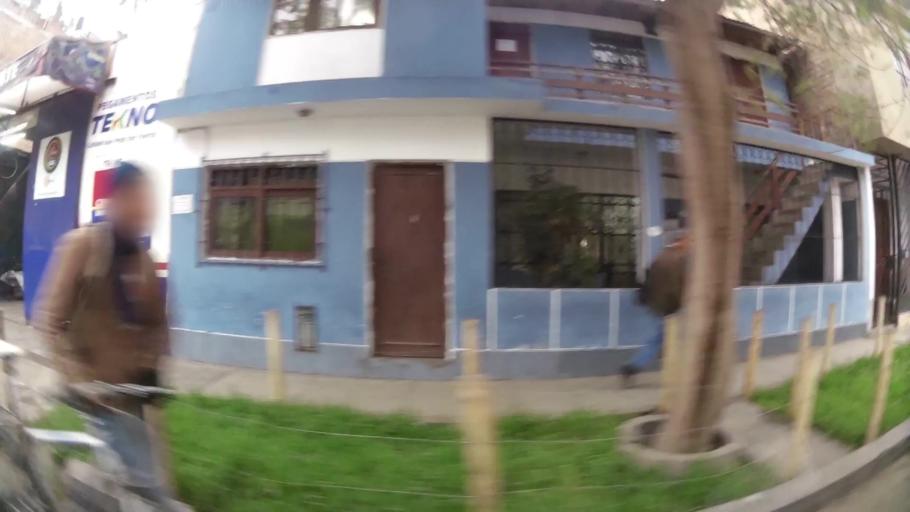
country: PE
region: Lima
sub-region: Lima
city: Surco
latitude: -12.1527
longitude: -76.9730
